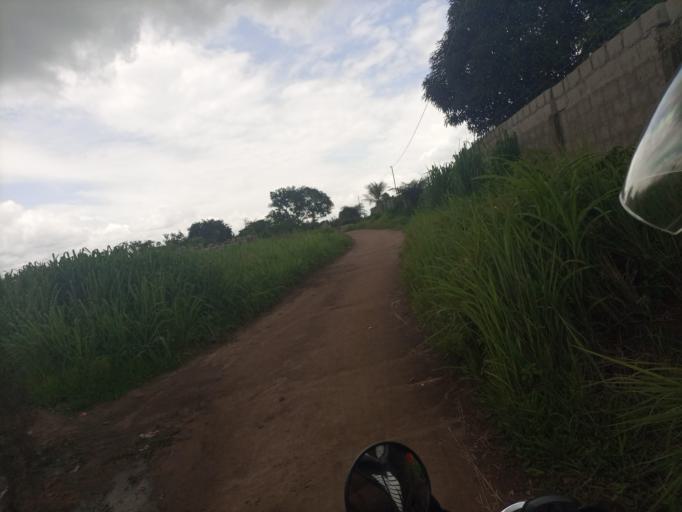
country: SL
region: Northern Province
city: Masoyila
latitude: 8.5791
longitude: -13.1604
